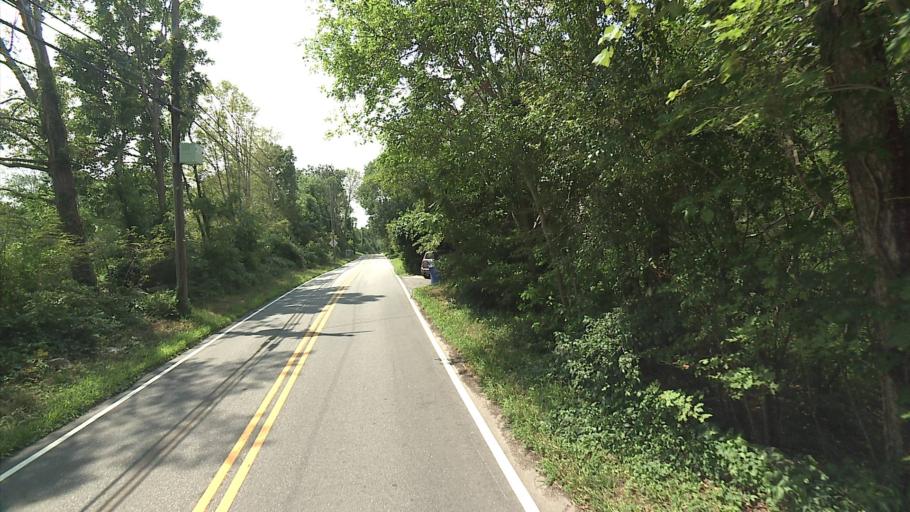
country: US
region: Connecticut
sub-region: Windham County
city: Danielson
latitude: 41.7717
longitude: -71.8437
